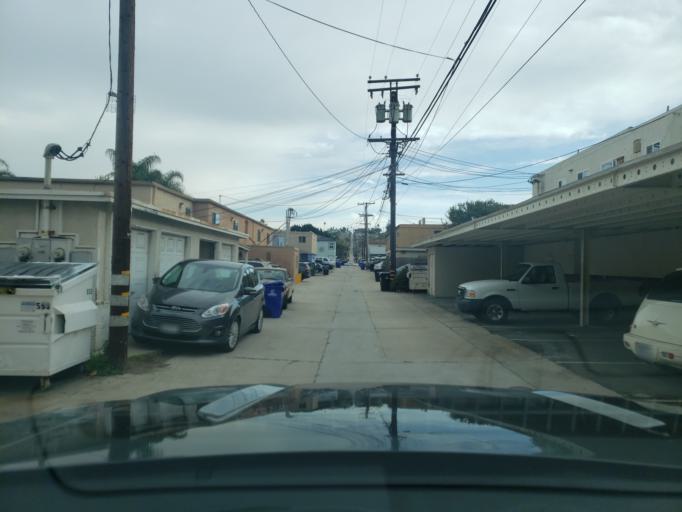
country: US
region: California
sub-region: San Diego County
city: Coronado
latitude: 32.7446
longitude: -117.2526
